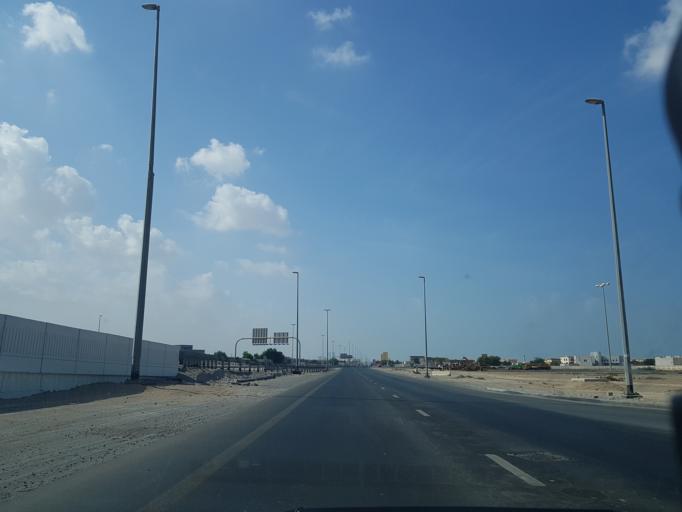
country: AE
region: Ra's al Khaymah
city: Ras al-Khaimah
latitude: 25.8340
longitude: 56.0132
